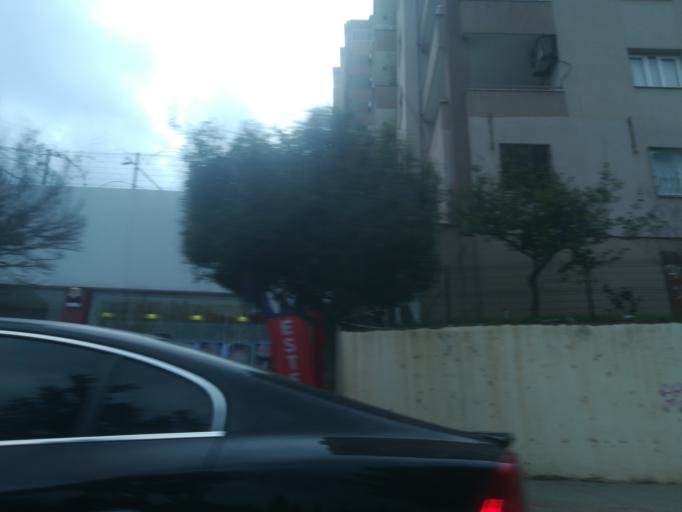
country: TR
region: Adana
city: Adana
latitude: 37.0381
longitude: 35.2934
